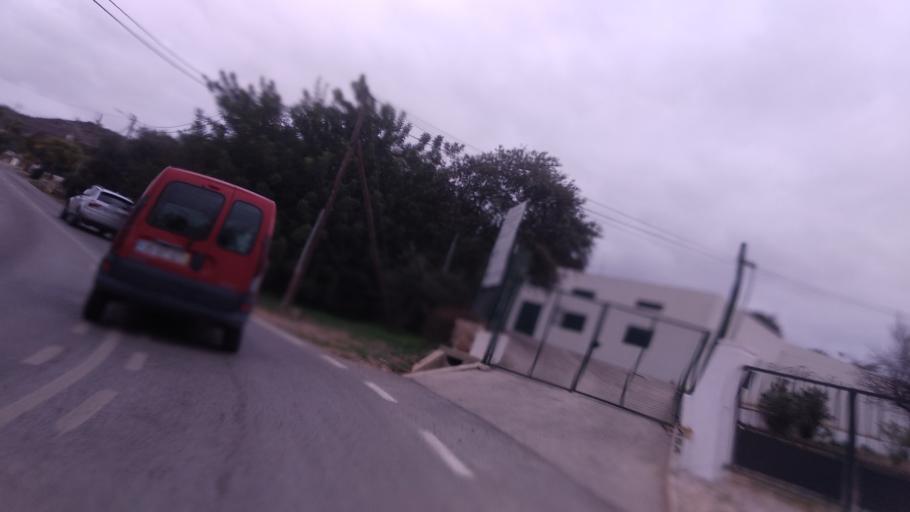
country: PT
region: Faro
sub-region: Faro
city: Santa Barbara de Nexe
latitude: 37.1086
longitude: -7.9617
